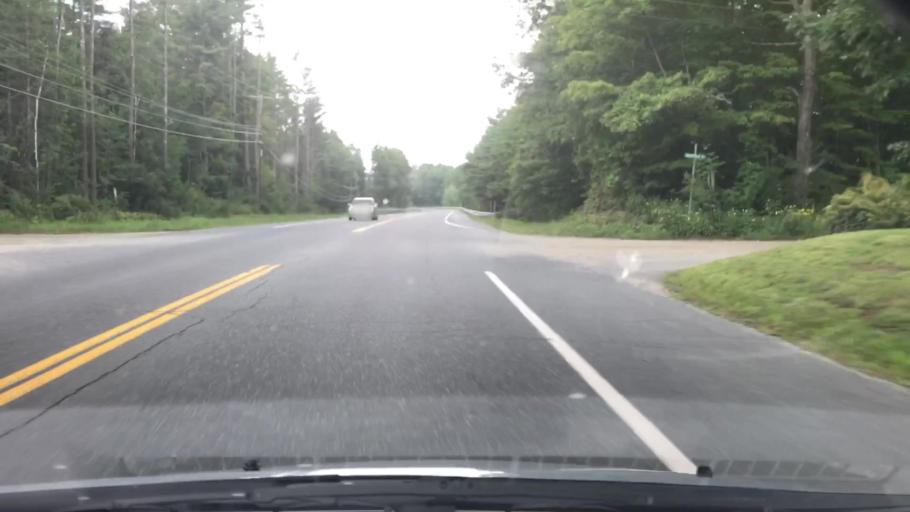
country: US
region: New Hampshire
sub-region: Grafton County
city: Lyme
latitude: 43.7834
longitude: -72.1775
